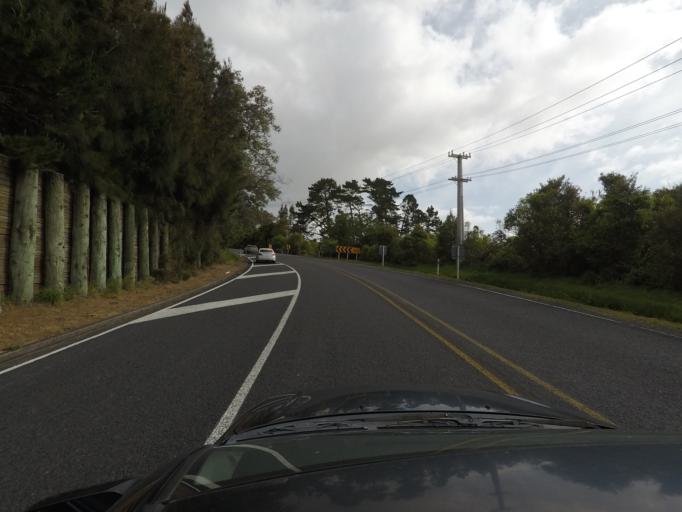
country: NZ
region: Auckland
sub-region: Auckland
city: Pakuranga
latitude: -36.9268
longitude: 174.9355
